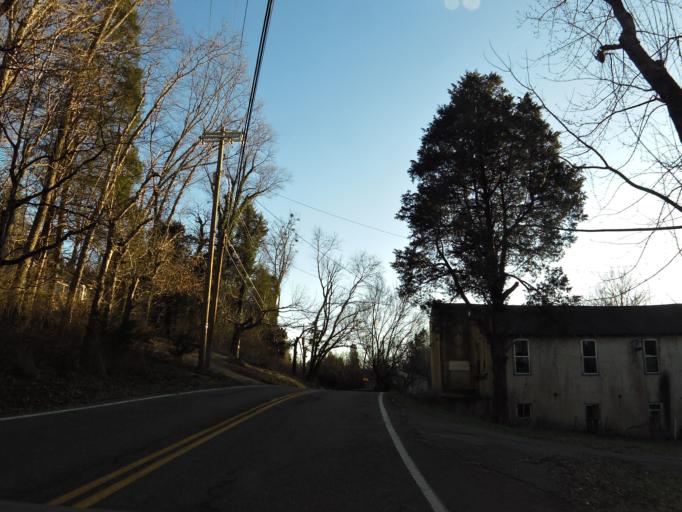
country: US
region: Tennessee
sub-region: Knox County
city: Knoxville
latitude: 35.9428
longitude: -83.8617
